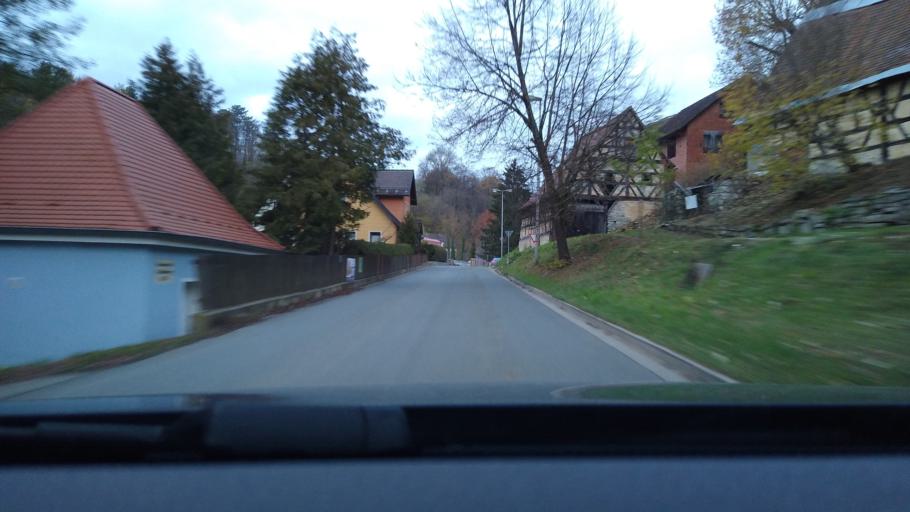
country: DE
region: Bavaria
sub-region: Upper Franconia
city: Grafenberg
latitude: 49.6481
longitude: 11.2491
